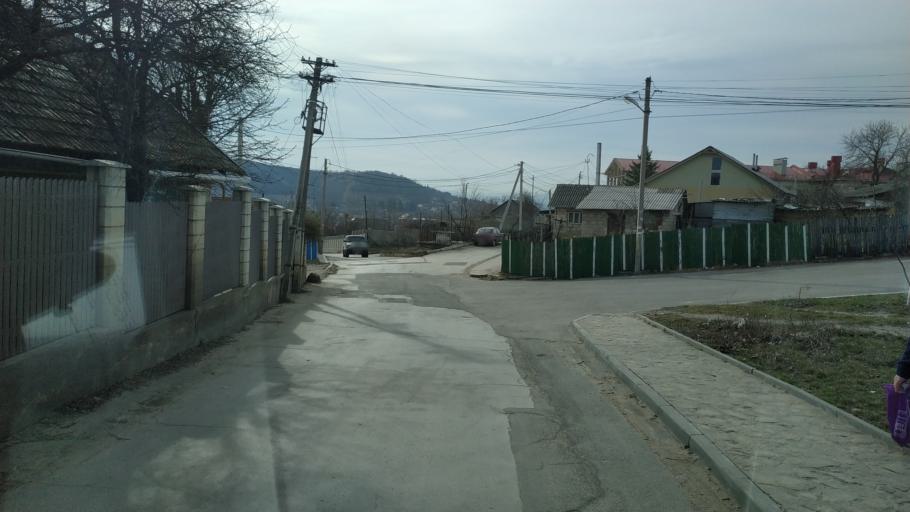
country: MD
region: Chisinau
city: Vatra
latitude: 47.0932
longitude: 28.7675
